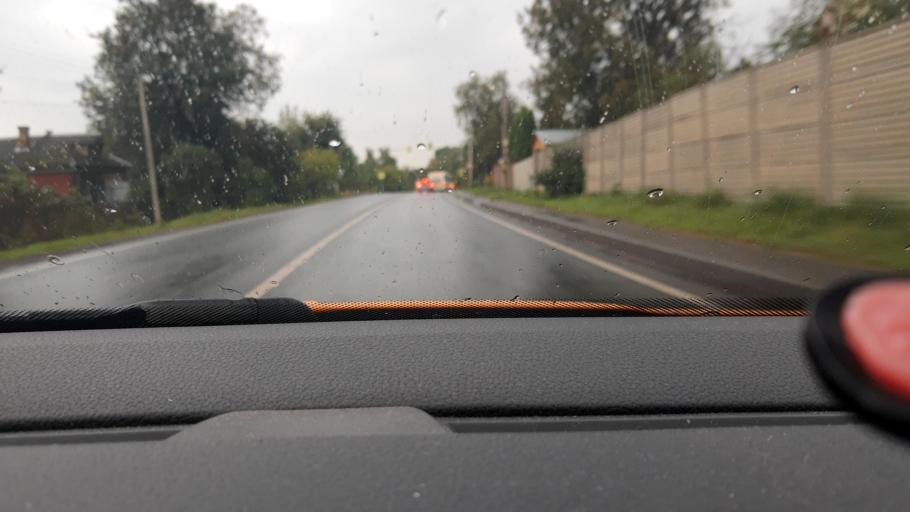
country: RU
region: Moskovskaya
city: Obukhovo
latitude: 55.8090
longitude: 38.2534
